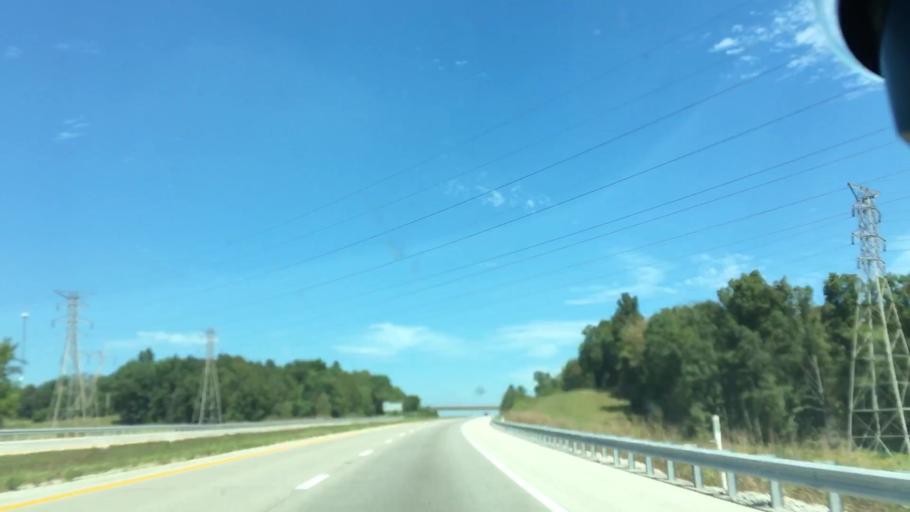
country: US
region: Kentucky
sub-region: Christian County
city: Hopkinsville
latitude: 36.9189
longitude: -87.4738
